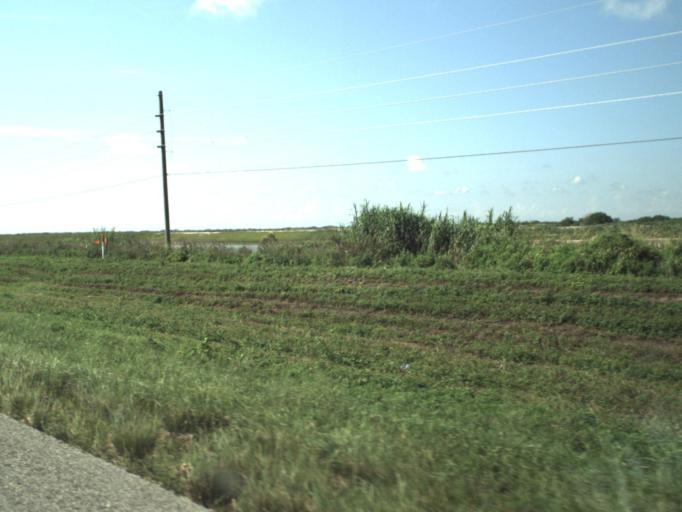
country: US
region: Florida
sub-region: Palm Beach County
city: Belle Glade Camp
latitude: 26.4636
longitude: -80.6377
